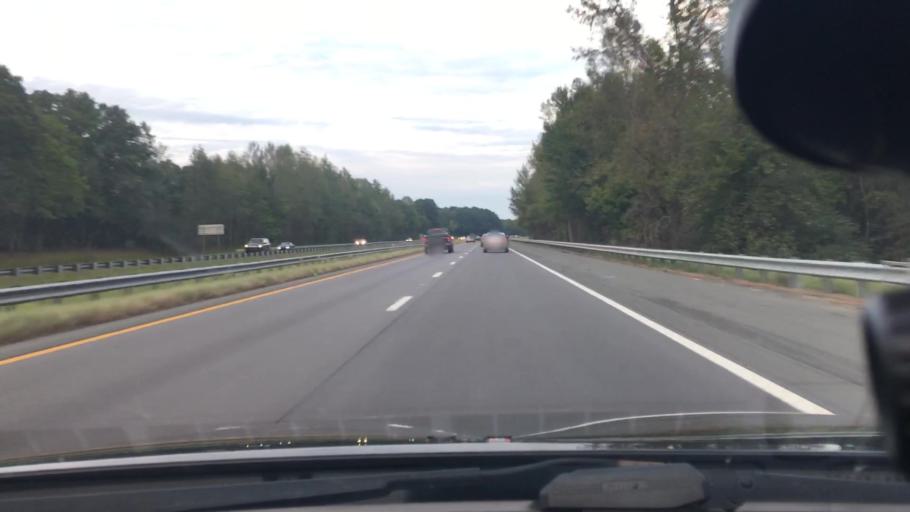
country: US
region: North Carolina
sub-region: Chatham County
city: Farmville
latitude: 35.6039
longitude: -79.1091
